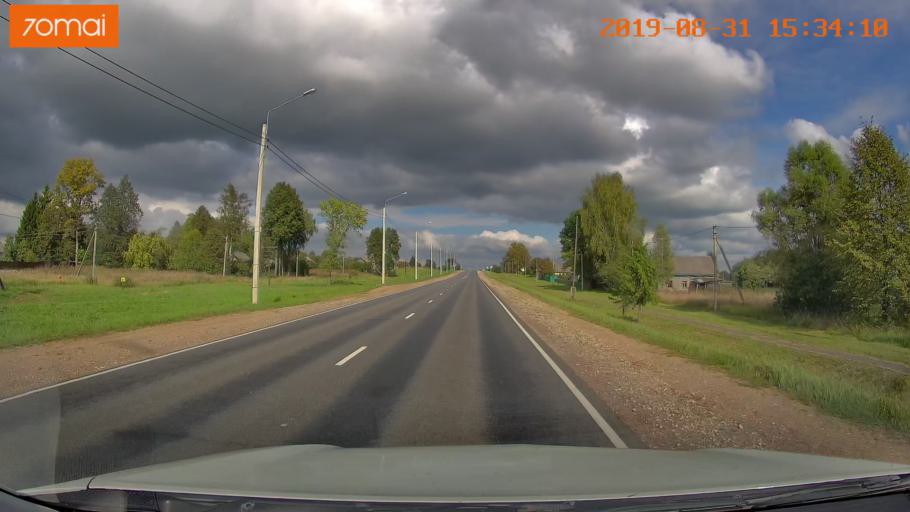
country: RU
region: Kaluga
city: Mosal'sk
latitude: 54.5992
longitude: 34.7154
